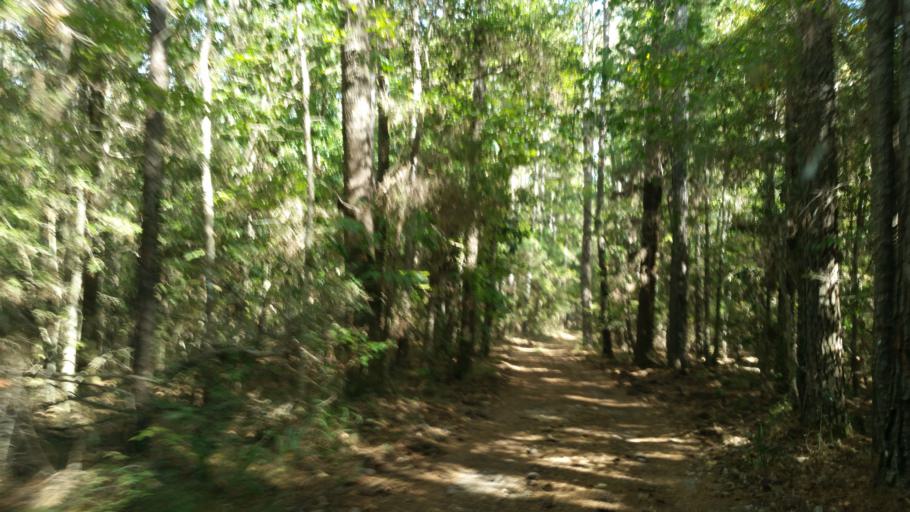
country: US
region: Alabama
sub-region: Baldwin County
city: Spanish Fort
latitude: 30.7373
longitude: -87.9209
